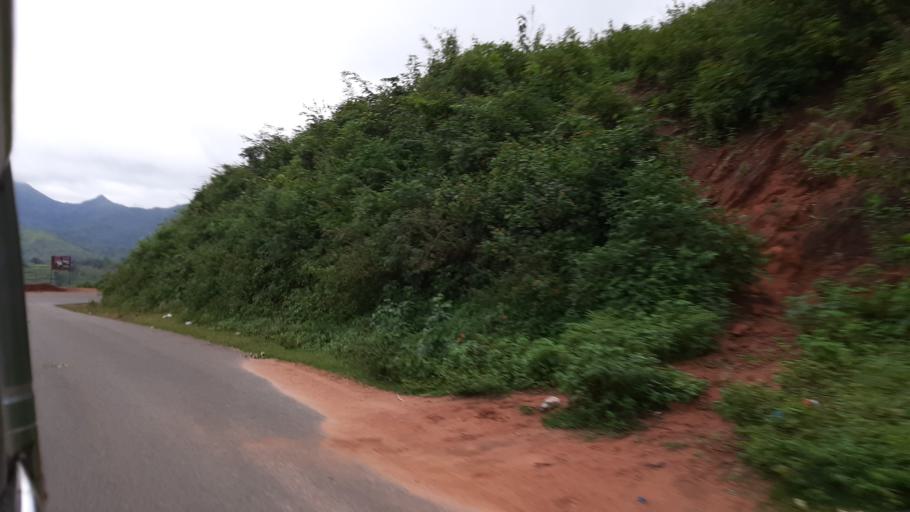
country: IN
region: Andhra Pradesh
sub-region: Vizianagaram District
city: Salur
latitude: 18.2846
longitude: 82.9460
